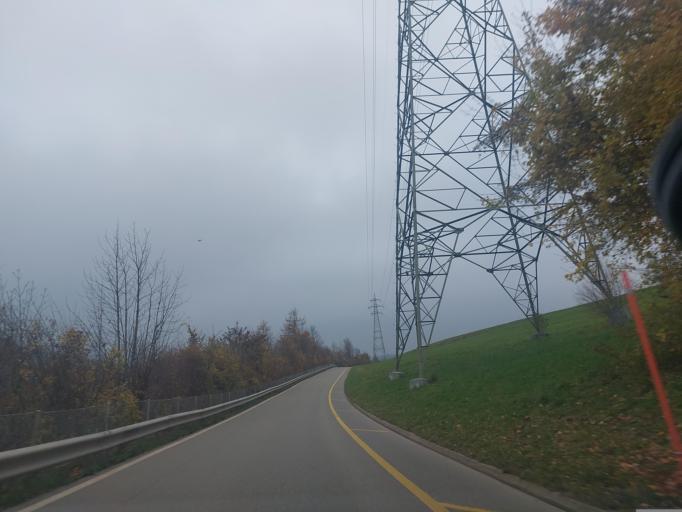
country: CH
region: Vaud
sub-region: Riviera-Pays-d'Enhaut District
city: Jongny
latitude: 46.4797
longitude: 6.8682
